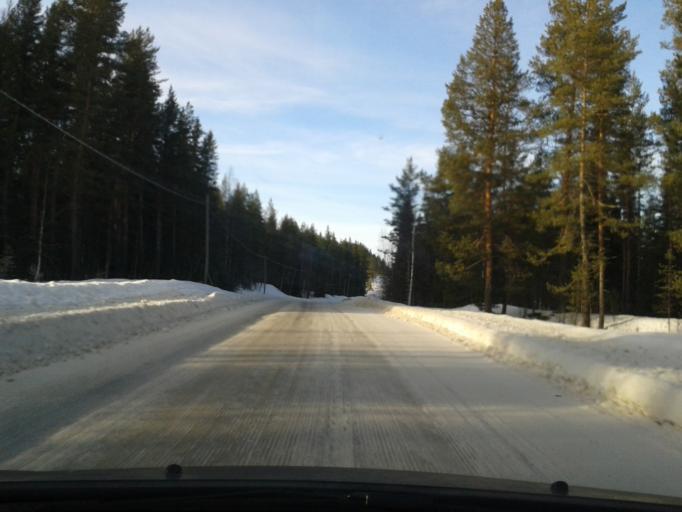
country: SE
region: Vaesternorrland
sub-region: OErnskoeldsviks Kommun
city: Bredbyn
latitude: 63.6667
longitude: 17.8320
